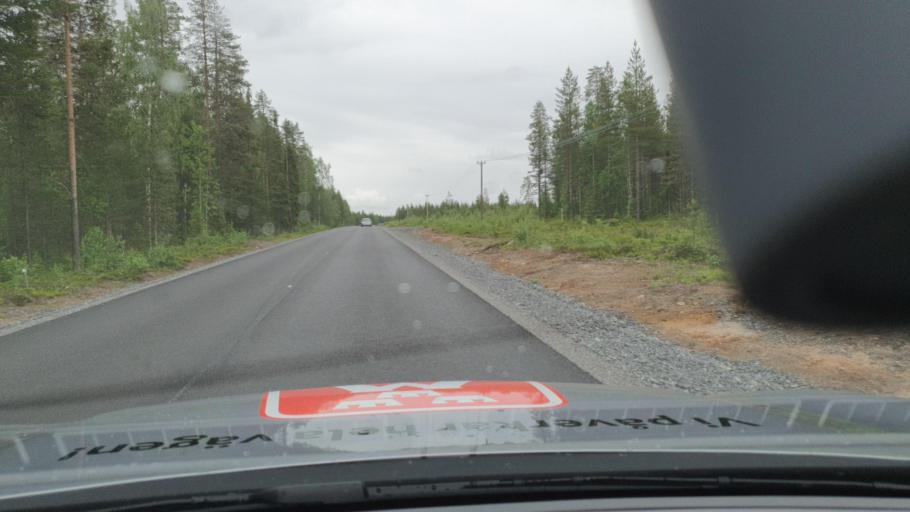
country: SE
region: Norrbotten
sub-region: Overkalix Kommun
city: OEverkalix
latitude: 66.6778
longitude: 23.2174
